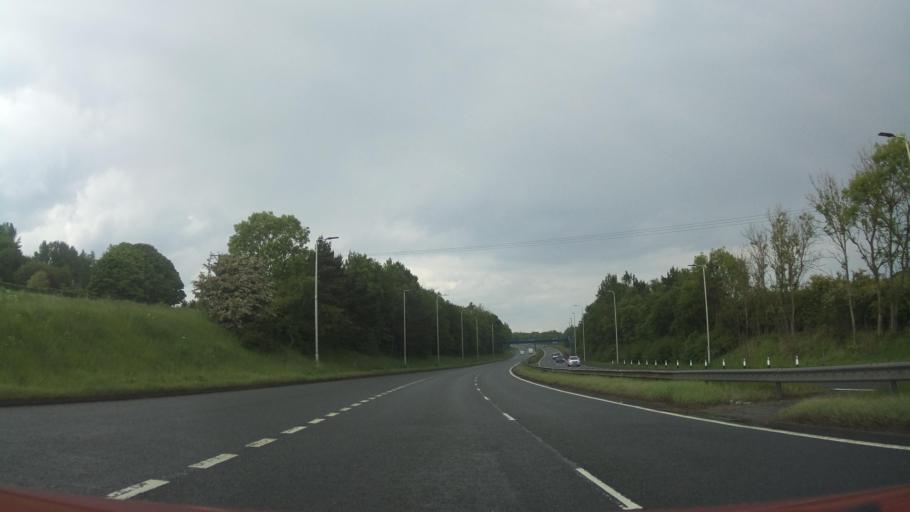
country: GB
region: England
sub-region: County Durham
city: Hawthorn
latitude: 54.8190
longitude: -1.3693
